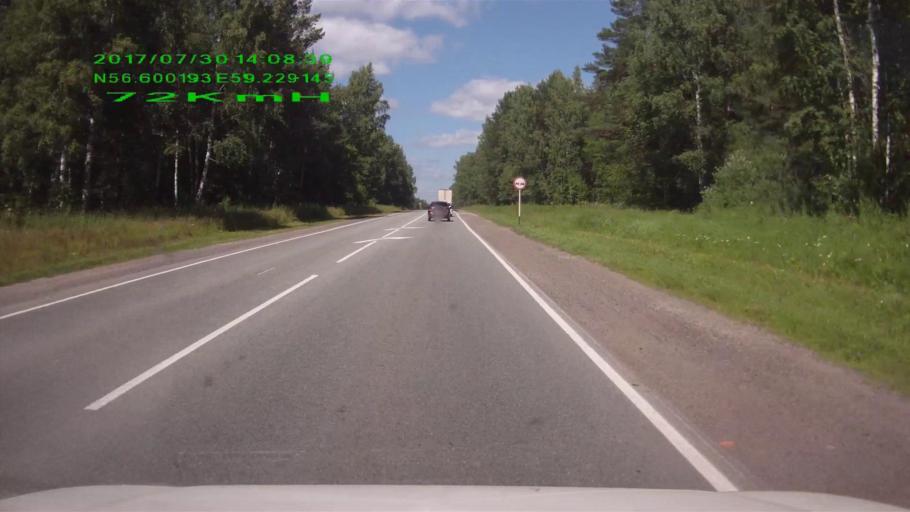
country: RU
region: Sverdlovsk
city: Nizhniye Sergi
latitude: 56.6003
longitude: 59.2291
